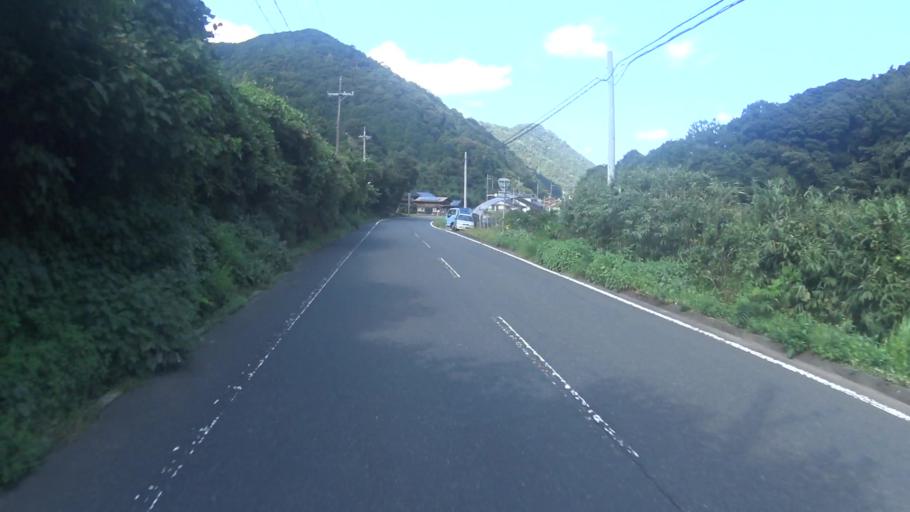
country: JP
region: Kyoto
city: Miyazu
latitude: 35.6936
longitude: 135.2775
